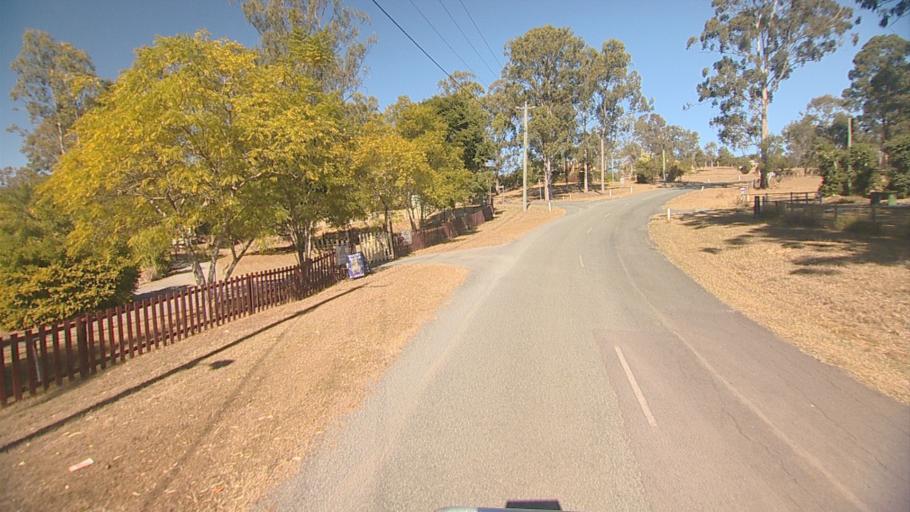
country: AU
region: Queensland
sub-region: Logan
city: Cedar Vale
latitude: -27.8856
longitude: 153.0000
